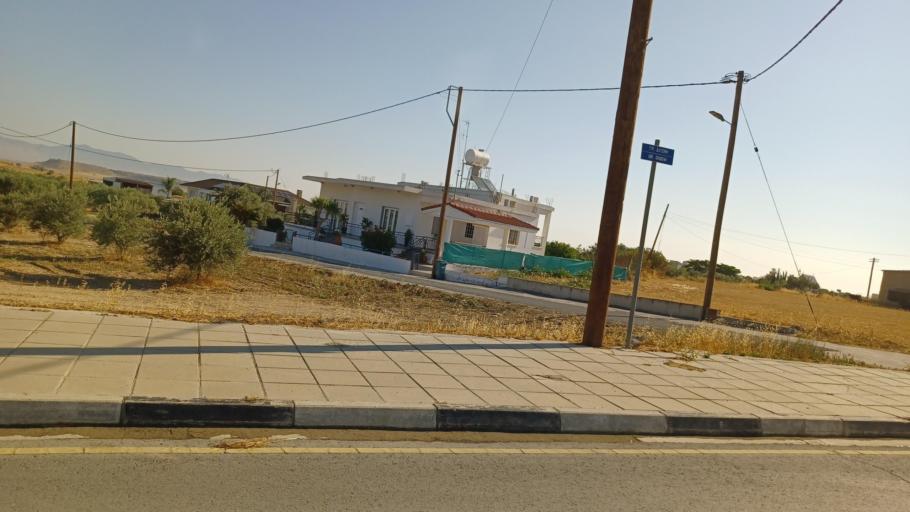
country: CY
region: Larnaka
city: Athienou
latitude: 35.0655
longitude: 33.5473
